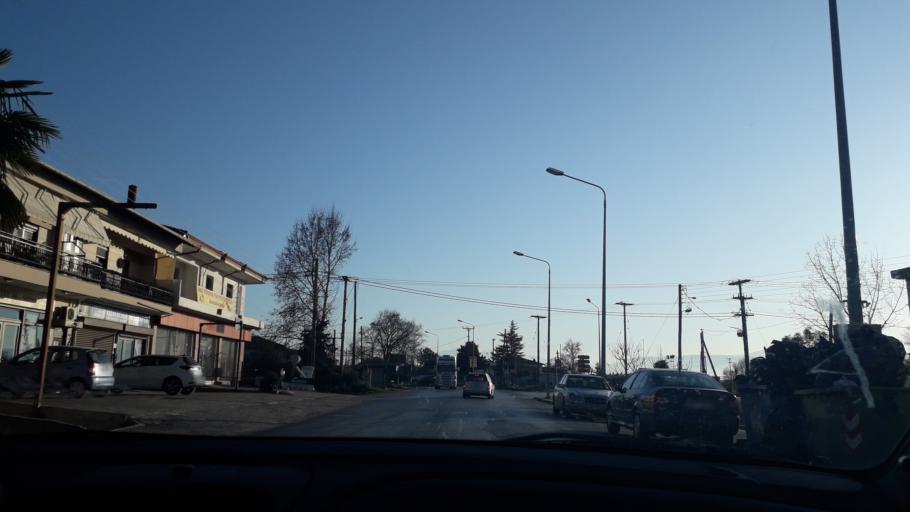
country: GR
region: Central Macedonia
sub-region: Nomos Imathias
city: Alexandreia
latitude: 40.6220
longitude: 22.4474
